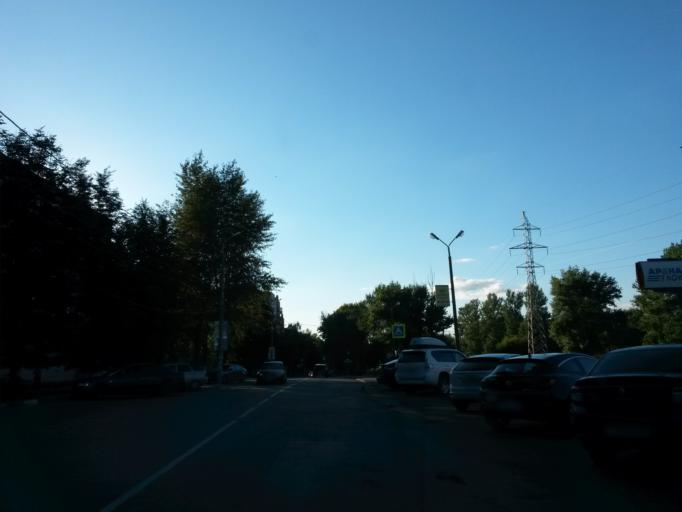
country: RU
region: Jaroslavl
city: Yaroslavl
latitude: 57.5849
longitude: 39.8435
